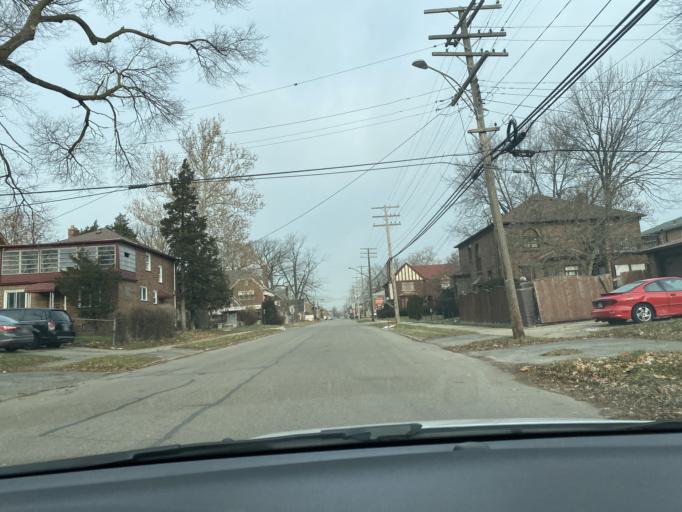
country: US
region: Michigan
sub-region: Wayne County
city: Highland Park
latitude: 42.3839
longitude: -83.1325
